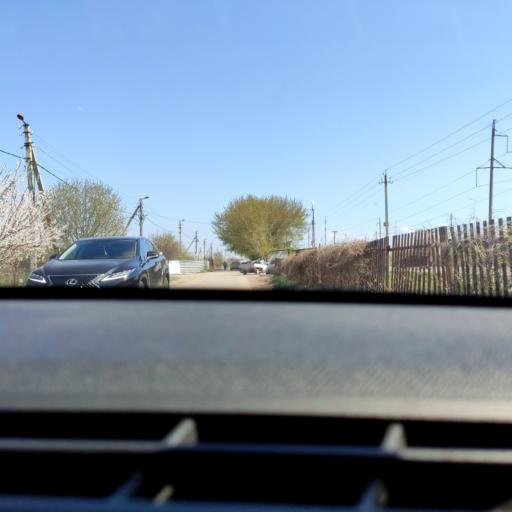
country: RU
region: Samara
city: Tol'yatti
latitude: 53.5905
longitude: 49.3077
